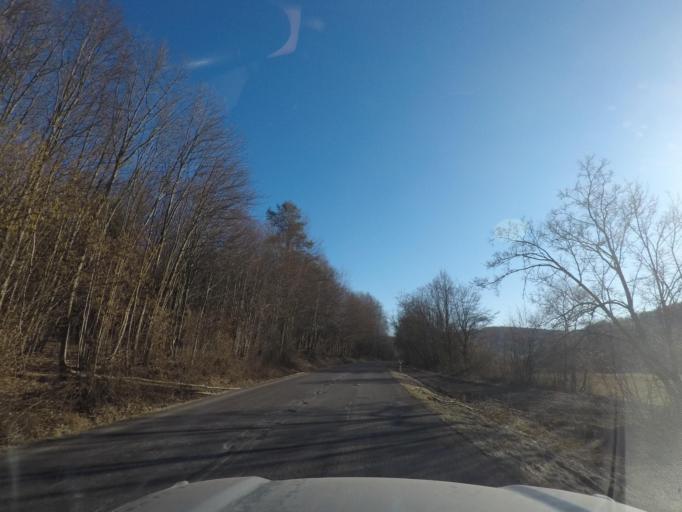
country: SK
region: Presovsky
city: Medzilaborce
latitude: 49.2657
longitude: 21.7981
